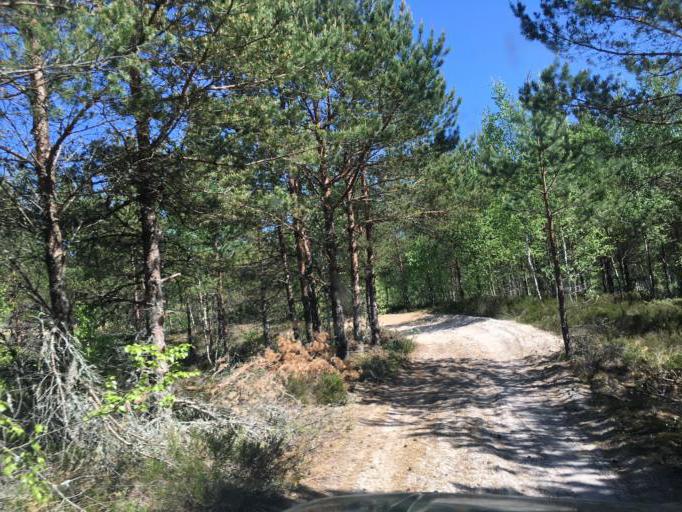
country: LV
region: Dundaga
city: Dundaga
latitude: 57.5675
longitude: 21.9973
